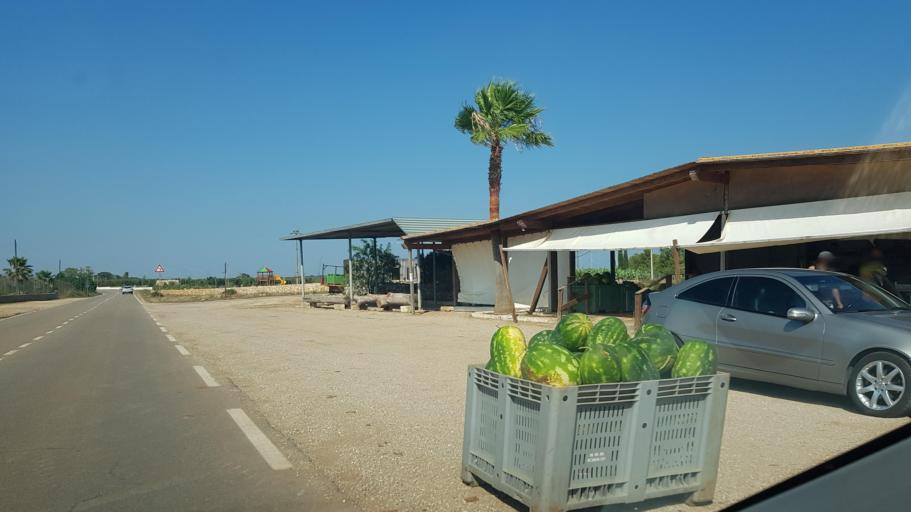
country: IT
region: Apulia
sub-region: Provincia di Lecce
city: Acquarica del Capo
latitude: 39.8720
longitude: 18.2224
